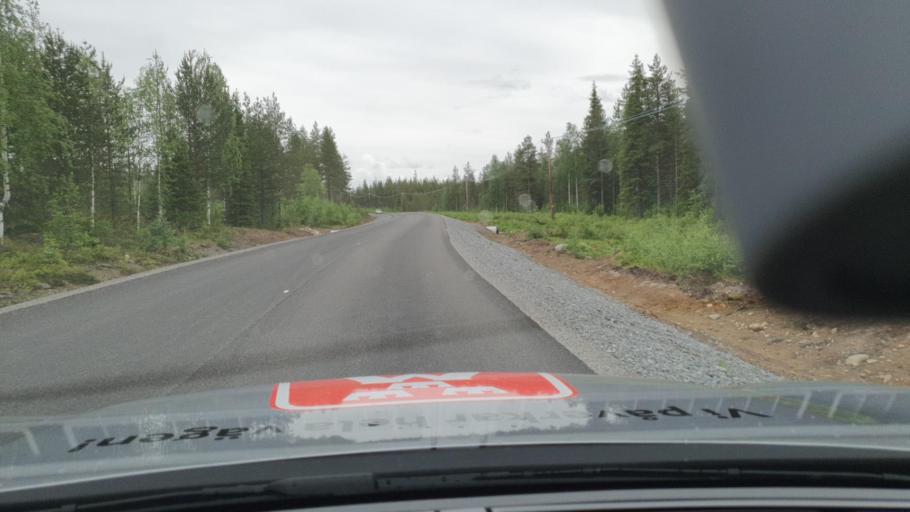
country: SE
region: Norrbotten
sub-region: Overtornea Kommun
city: OEvertornea
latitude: 66.6413
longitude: 23.2520
